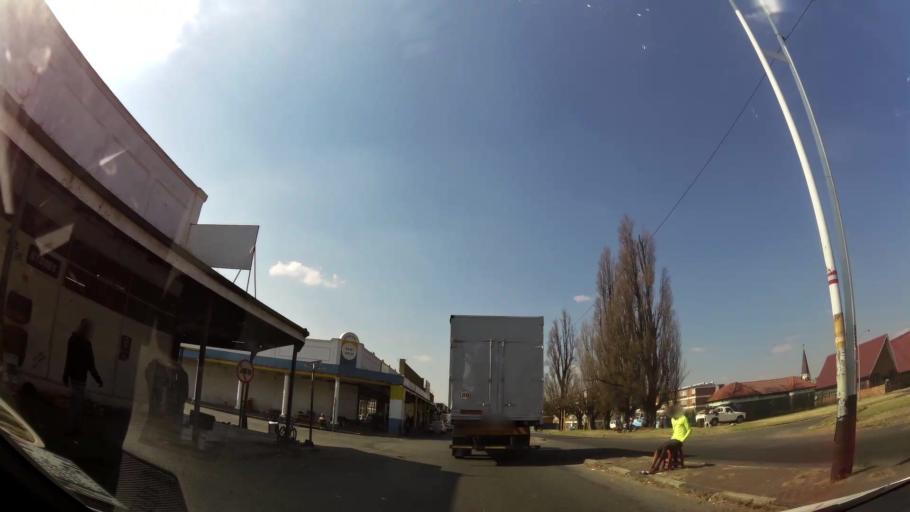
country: ZA
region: Gauteng
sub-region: Ekurhuleni Metropolitan Municipality
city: Boksburg
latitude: -26.2087
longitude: 28.2559
